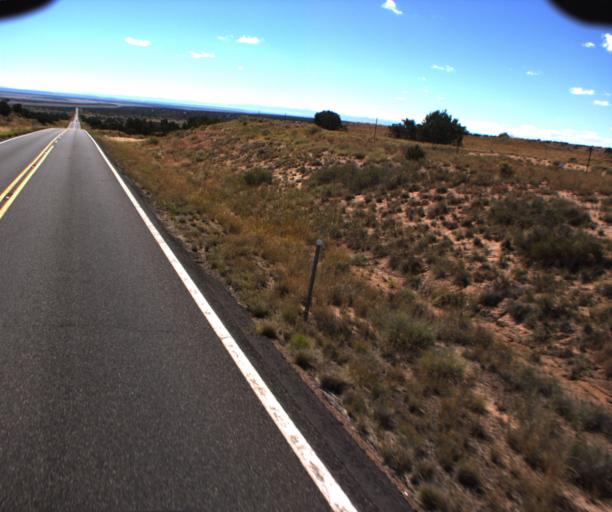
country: US
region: Arizona
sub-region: Apache County
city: Saint Johns
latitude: 34.8221
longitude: -109.2375
